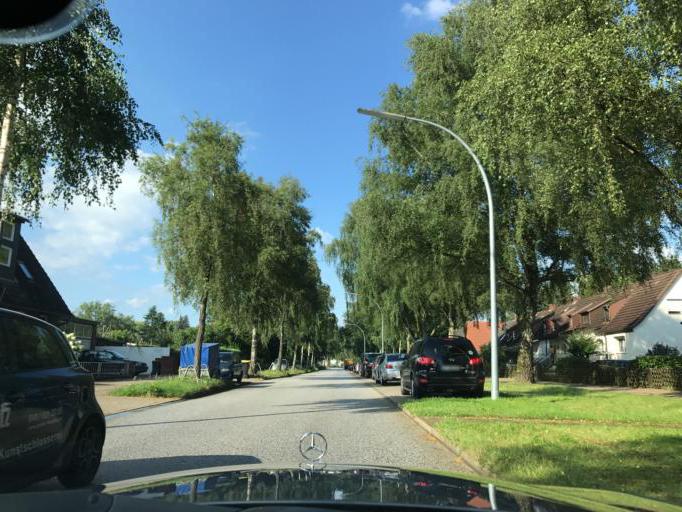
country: DE
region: Hamburg
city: Wandsbek
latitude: 53.5536
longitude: 10.1040
